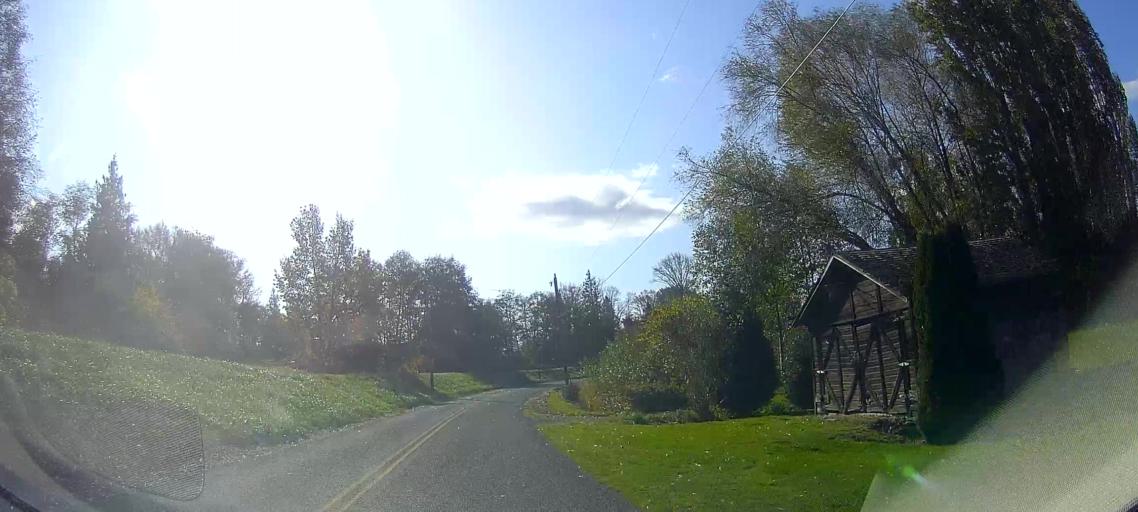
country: US
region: Washington
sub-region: Snohomish County
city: Stanwood
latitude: 48.3290
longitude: -122.3535
